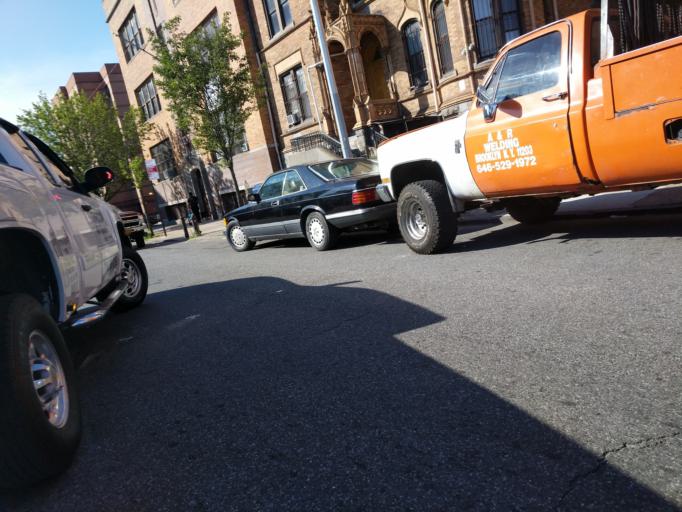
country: US
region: New York
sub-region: Queens County
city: Long Island City
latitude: 40.7008
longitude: -73.9447
